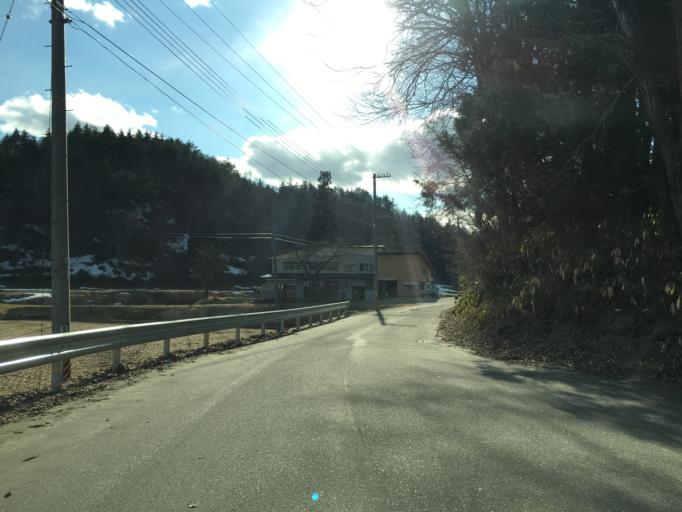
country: JP
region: Yamagata
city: Yonezawa
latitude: 37.9295
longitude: 139.9638
